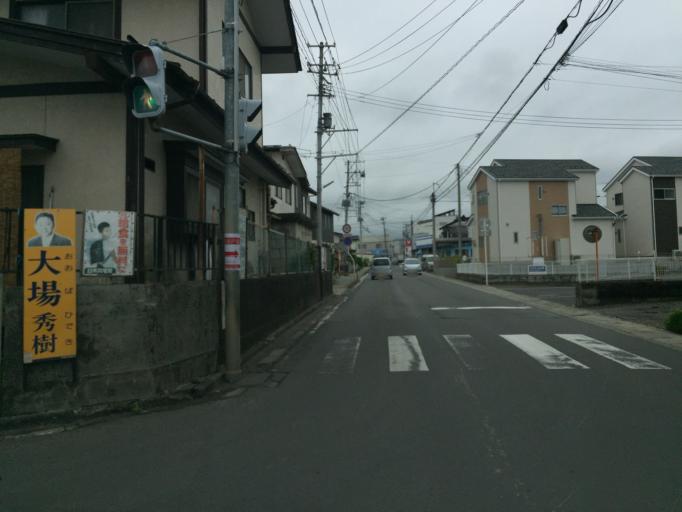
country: JP
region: Fukushima
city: Fukushima-shi
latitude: 37.7694
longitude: 140.4283
